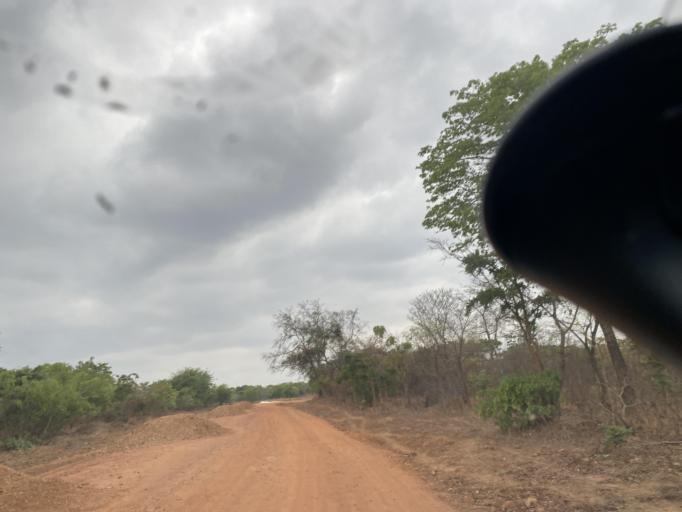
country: ZM
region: Lusaka
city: Chongwe
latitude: -15.2254
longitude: 28.7398
